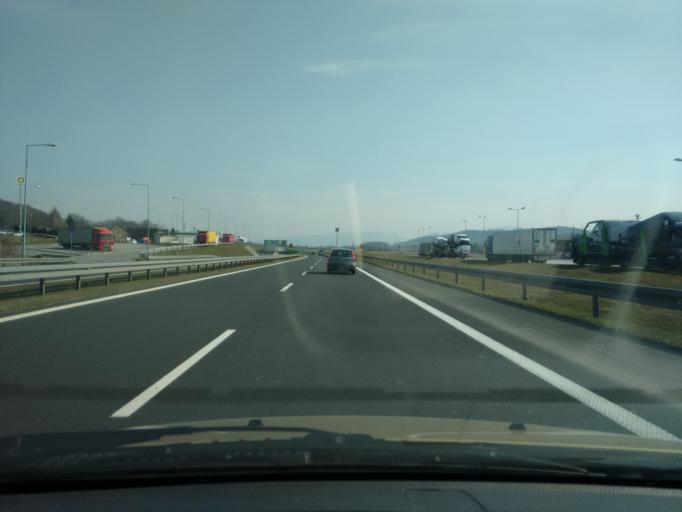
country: PL
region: Silesian Voivodeship
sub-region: Powiat cieszynski
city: Bazanowice
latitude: 49.7650
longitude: 18.6988
